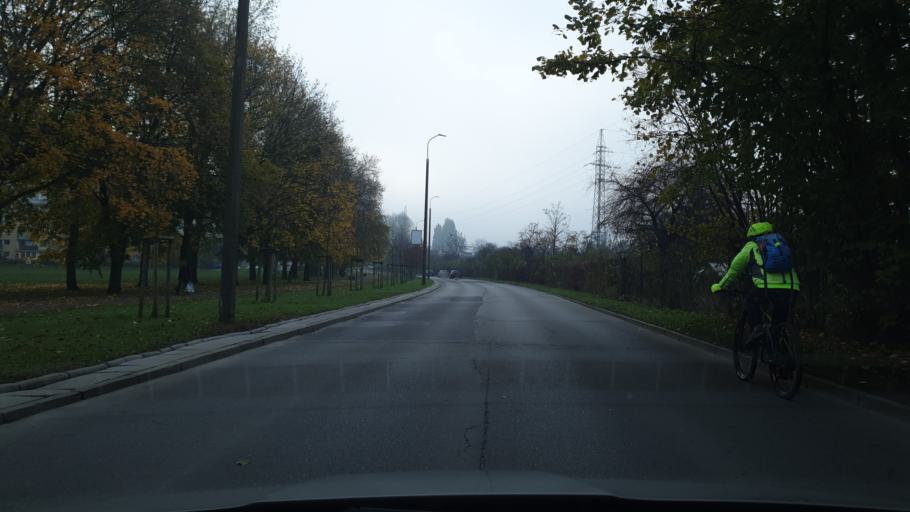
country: PL
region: Pomeranian Voivodeship
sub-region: Sopot
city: Sopot
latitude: 54.3936
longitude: 18.5878
